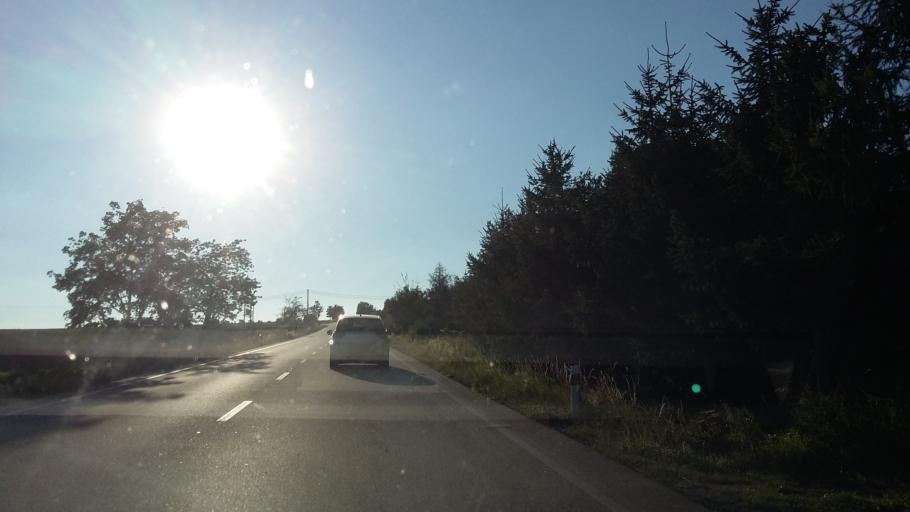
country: CZ
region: Vysocina
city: Velky Beranov
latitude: 49.4020
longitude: 15.6695
